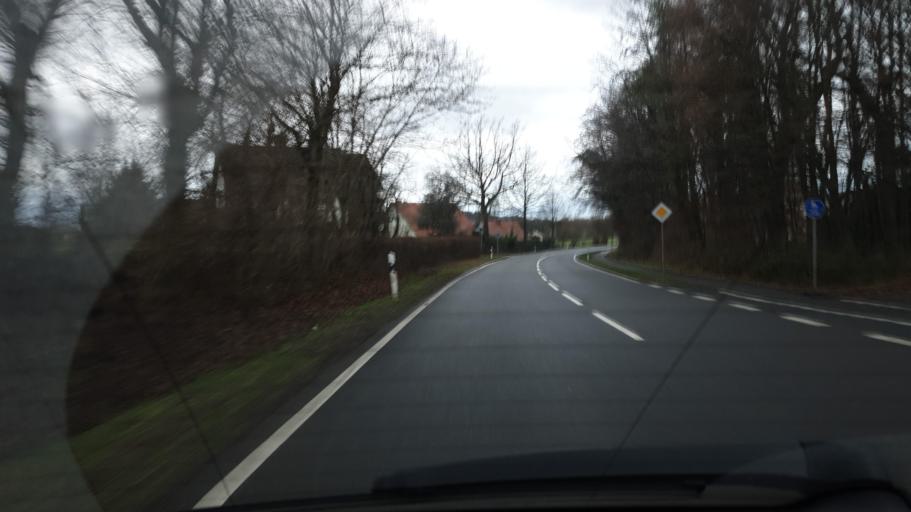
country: DE
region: North Rhine-Westphalia
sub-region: Regierungsbezirk Detmold
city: Vlotho
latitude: 52.1278
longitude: 8.8390
